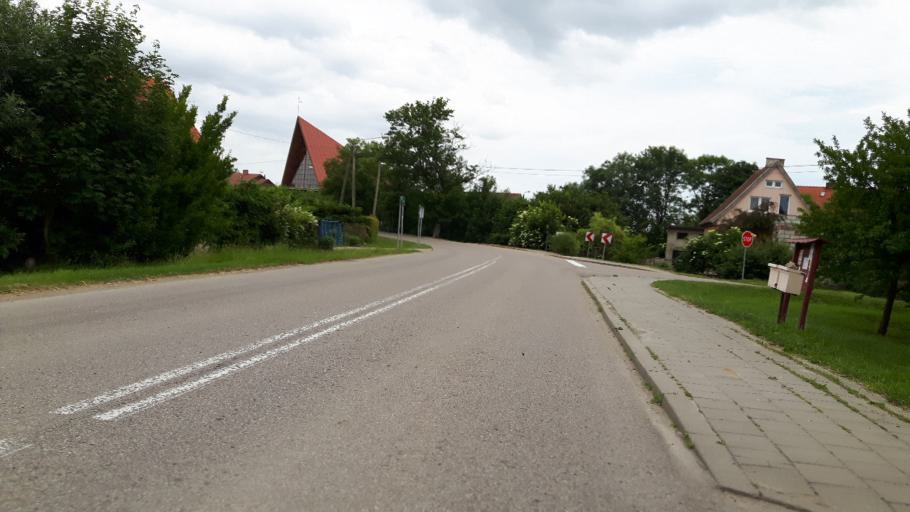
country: PL
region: Warmian-Masurian Voivodeship
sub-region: Powiat elblaski
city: Gronowo Elblaskie
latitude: 54.1908
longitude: 19.2979
